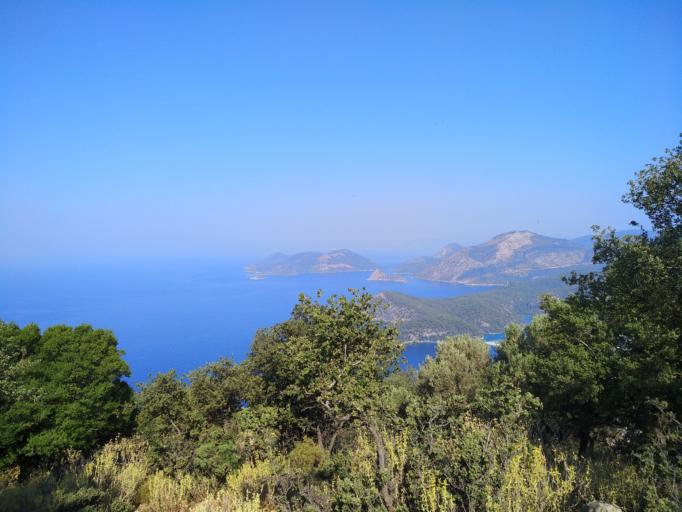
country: TR
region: Mugla
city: OEluedeniz
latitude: 36.5399
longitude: 29.1352
